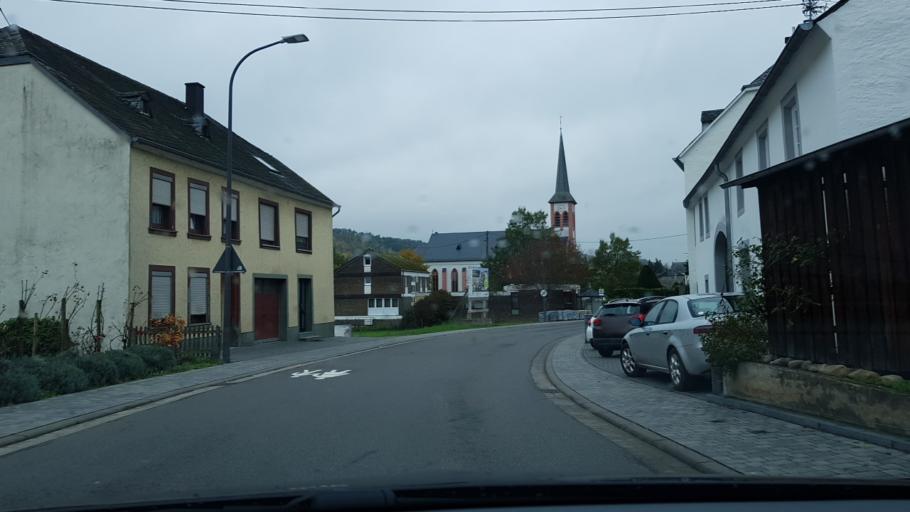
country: DE
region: Rheinland-Pfalz
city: Fell
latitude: 49.7764
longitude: 6.7790
